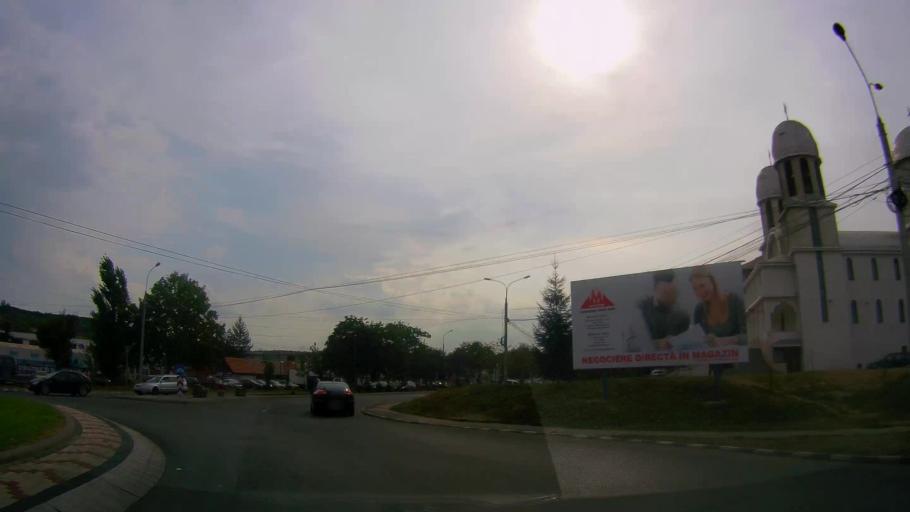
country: RO
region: Salaj
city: Zalau
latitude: 47.2028
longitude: 23.0518
